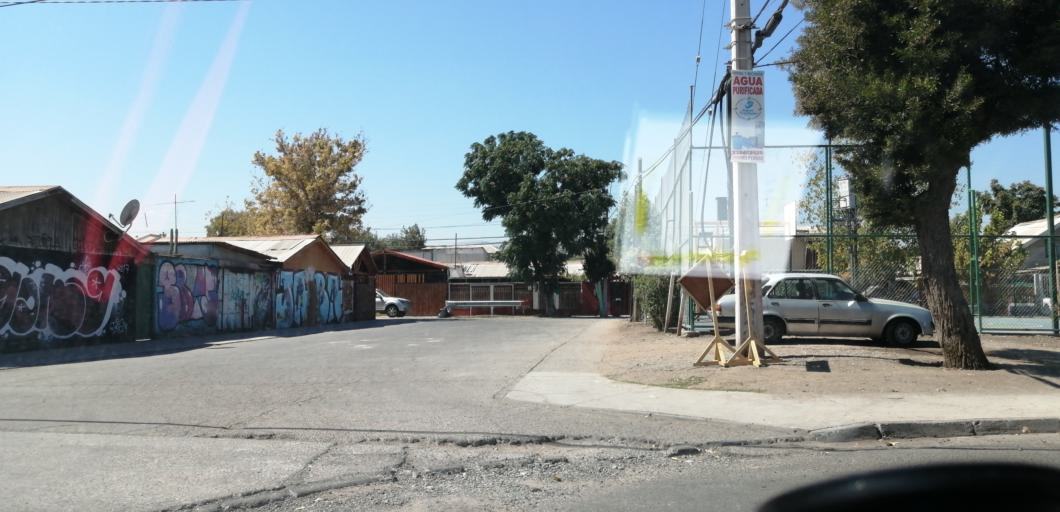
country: CL
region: Santiago Metropolitan
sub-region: Provincia de Santiago
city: Lo Prado
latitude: -33.4337
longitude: -70.7530
